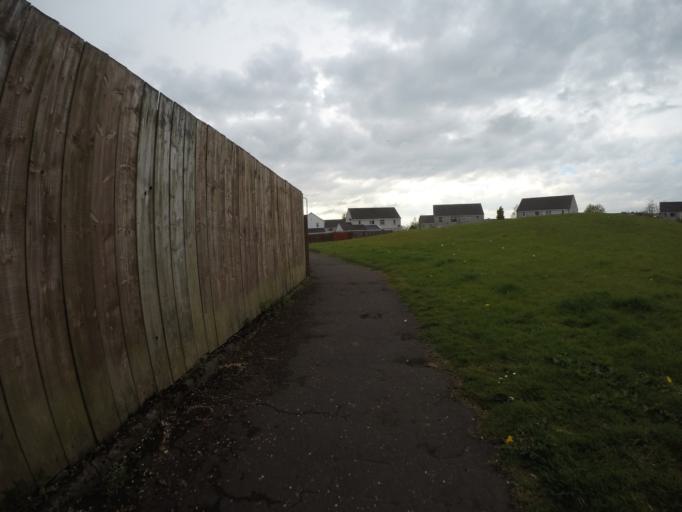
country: GB
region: Scotland
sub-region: East Ayrshire
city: Kilmaurs
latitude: 55.6405
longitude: -4.5367
